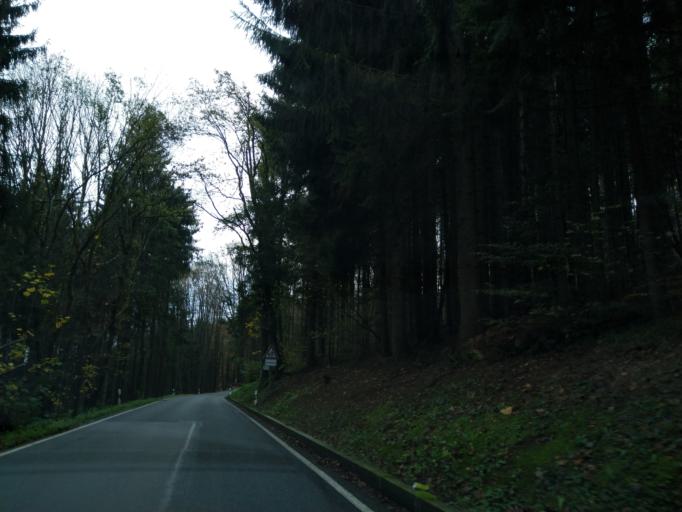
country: DE
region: Bavaria
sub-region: Lower Bavaria
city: Schofweg
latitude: 48.8037
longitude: 13.2269
